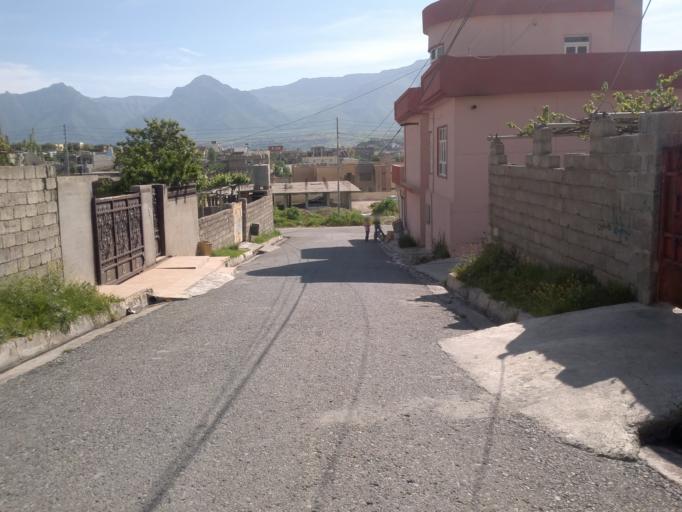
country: IQ
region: Arbil
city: Soran
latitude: 36.6501
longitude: 44.5524
